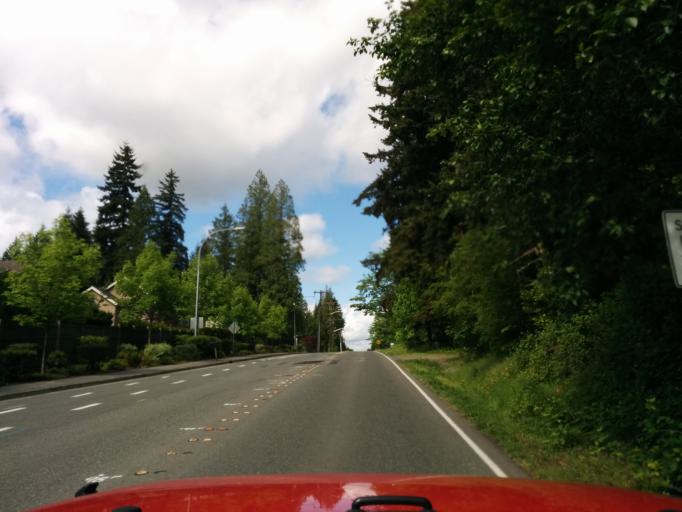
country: US
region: Washington
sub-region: King County
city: Redmond
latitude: 47.7039
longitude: -122.1114
